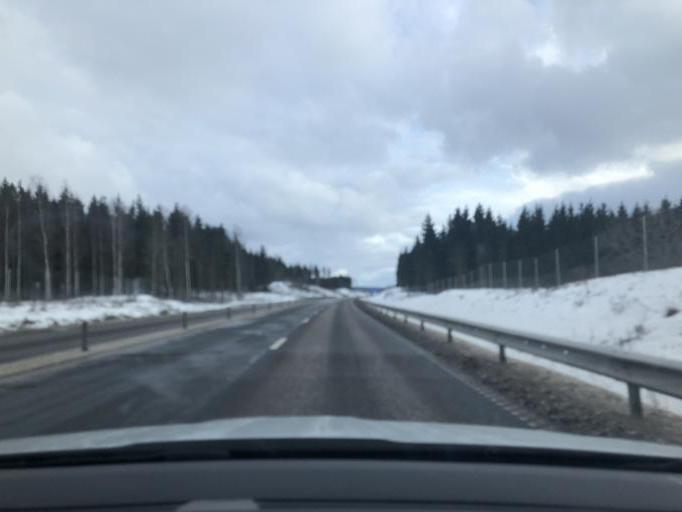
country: SE
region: OEstergoetland
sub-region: Motala Kommun
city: Borensberg
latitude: 58.5883
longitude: 15.1862
